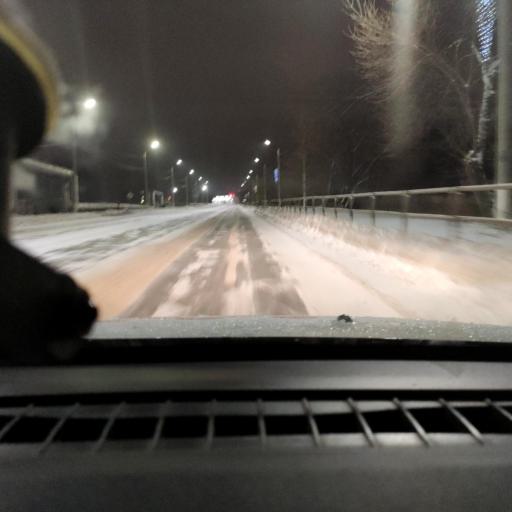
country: RU
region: Samara
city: Novokuybyshevsk
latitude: 53.0932
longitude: 49.9407
